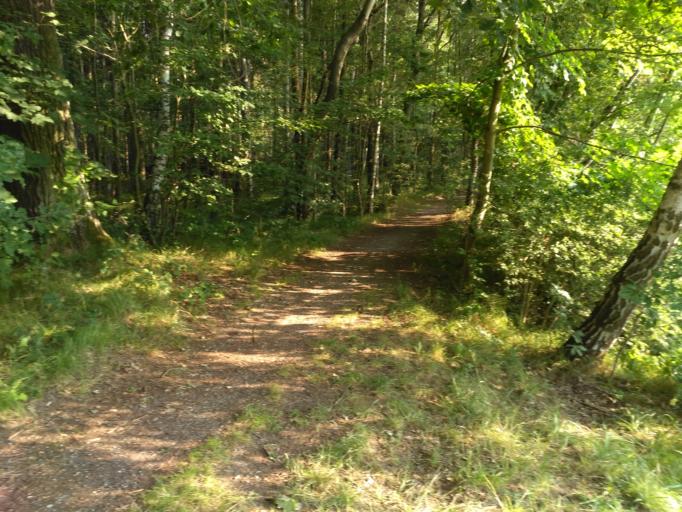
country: DE
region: Saxony
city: Demitz-Thumitz
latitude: 51.1484
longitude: 14.2617
